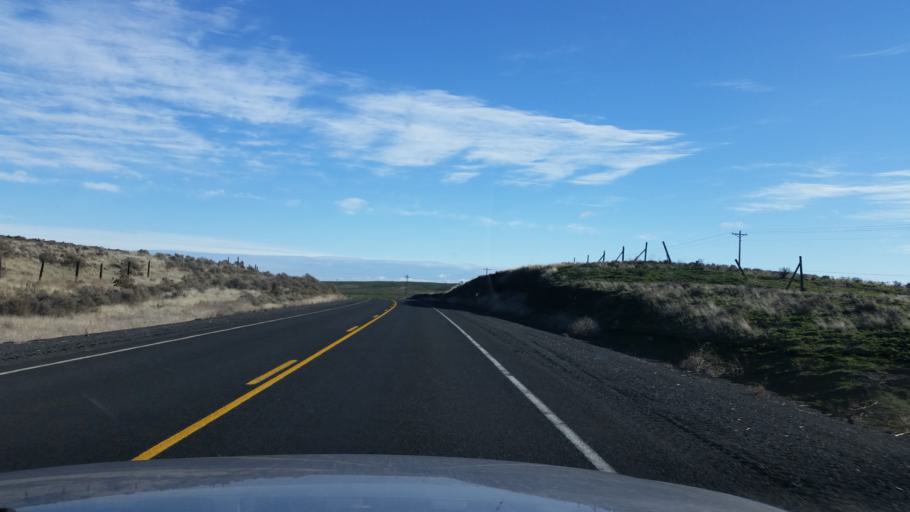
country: US
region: Washington
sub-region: Grant County
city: Warden
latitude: 47.3190
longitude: -118.8557
